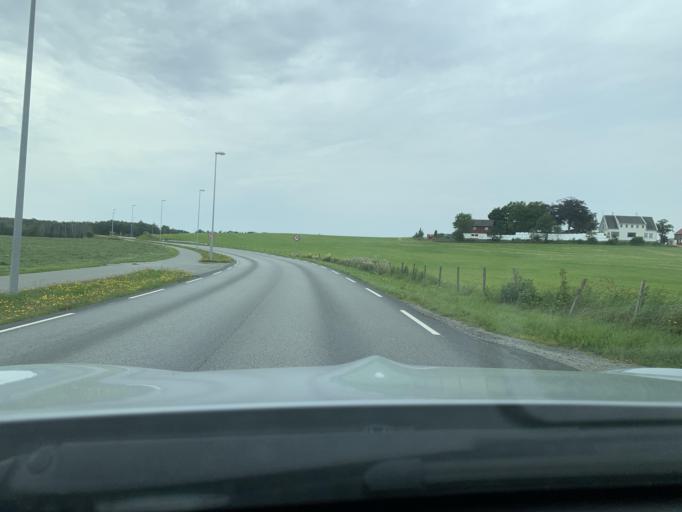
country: NO
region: Rogaland
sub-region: Time
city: Bryne
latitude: 58.7658
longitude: 5.7165
